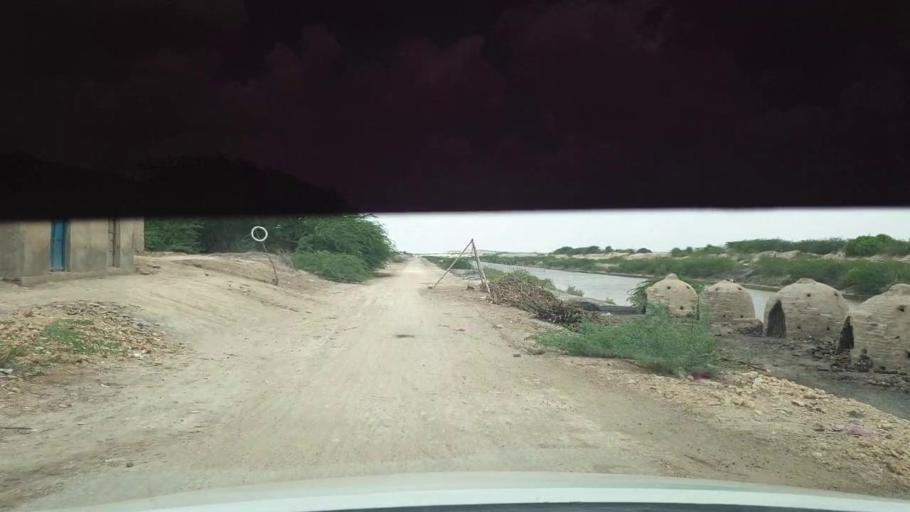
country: PK
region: Sindh
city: Kadhan
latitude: 24.4989
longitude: 69.1077
